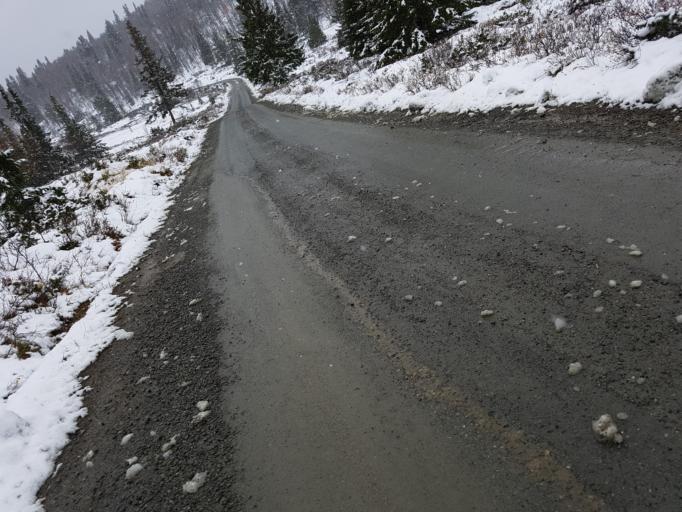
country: NO
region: Oppland
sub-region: Sel
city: Otta
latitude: 61.7966
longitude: 9.7148
